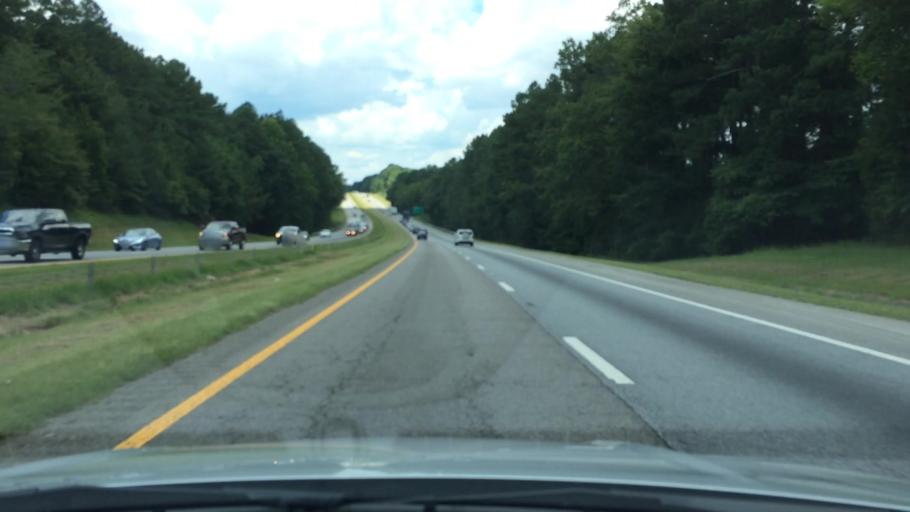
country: US
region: South Carolina
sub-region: Newberry County
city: Prosperity
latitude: 34.2737
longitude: -81.5143
